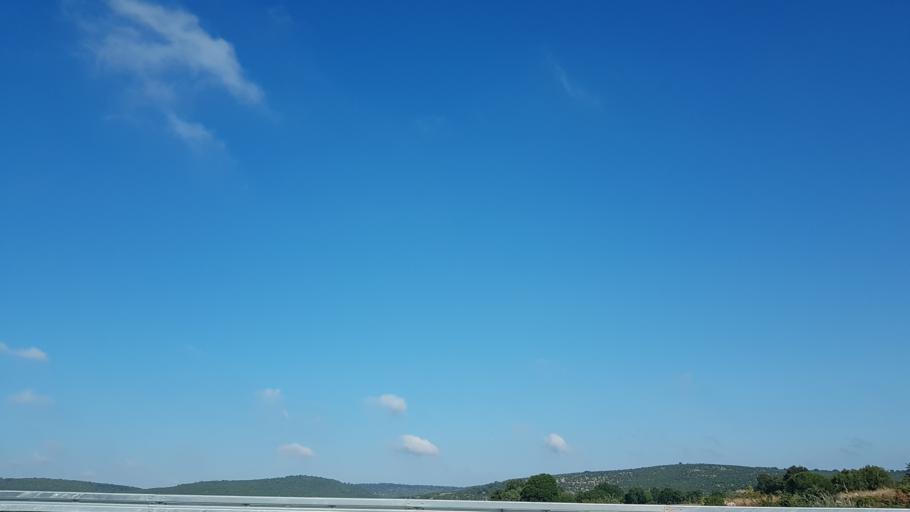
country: TR
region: Balikesir
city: Ertugrul
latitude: 39.5416
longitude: 27.6766
